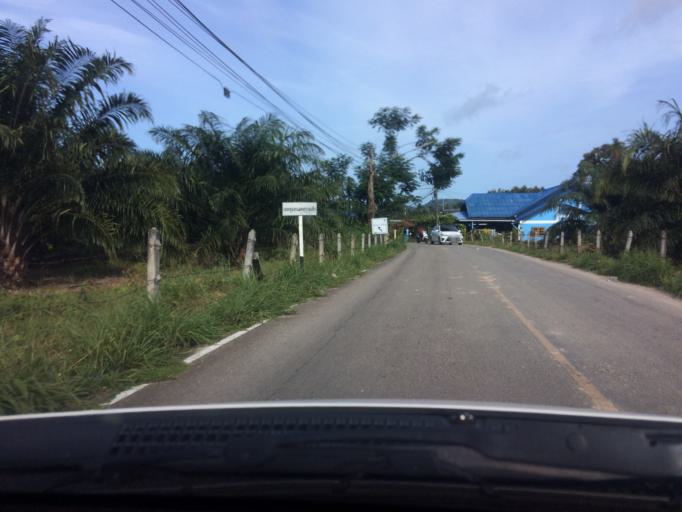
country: TH
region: Phuket
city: Thalang
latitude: 8.0438
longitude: 98.3302
